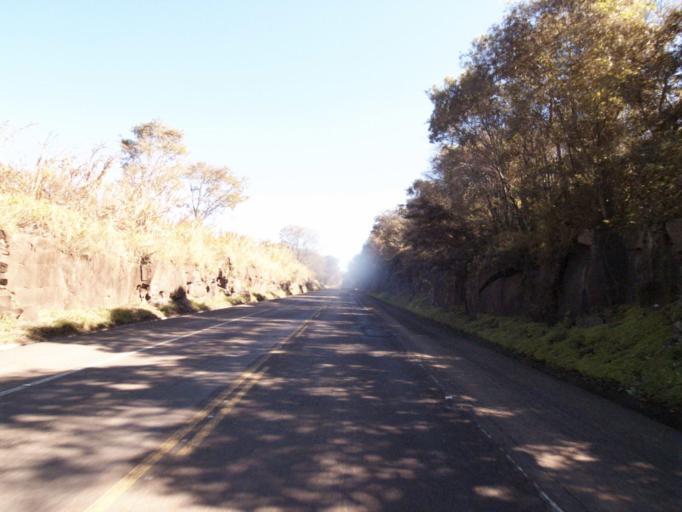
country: AR
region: Misiones
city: Bernardo de Irigoyen
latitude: -26.7685
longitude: -53.4676
